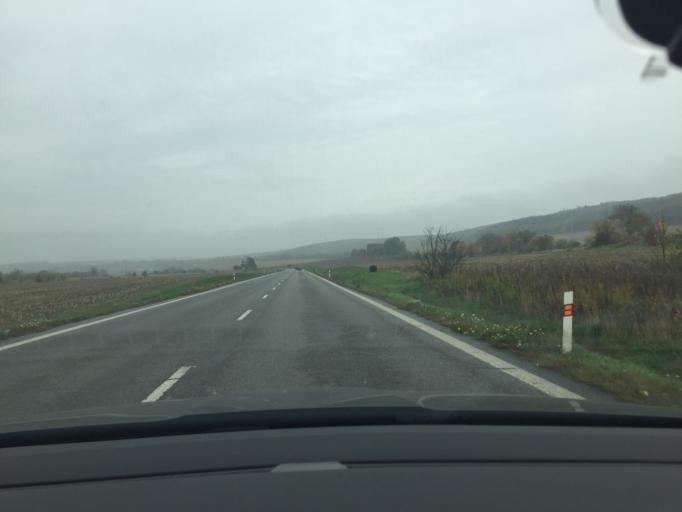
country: CZ
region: South Moravian
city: Nesovice
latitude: 49.1490
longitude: 17.0982
